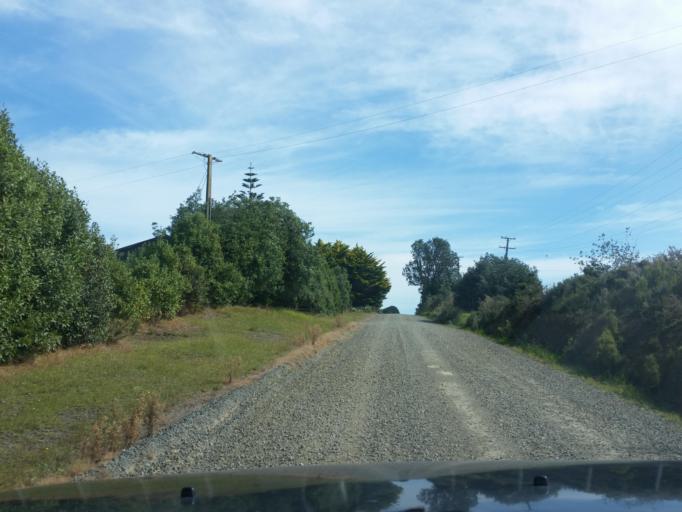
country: NZ
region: Northland
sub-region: Kaipara District
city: Dargaville
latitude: -35.9279
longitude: 173.7423
